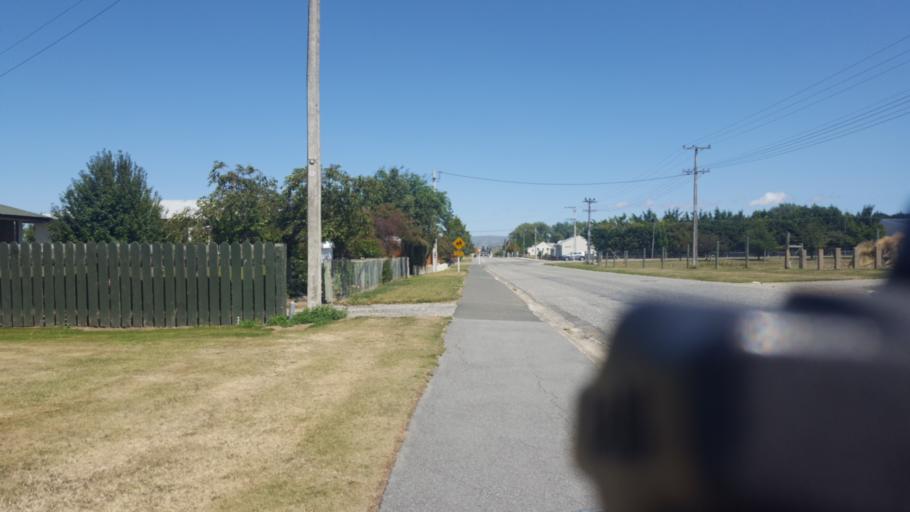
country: NZ
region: Otago
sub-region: Dunedin City
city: Dunedin
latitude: -45.1257
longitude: 170.1022
